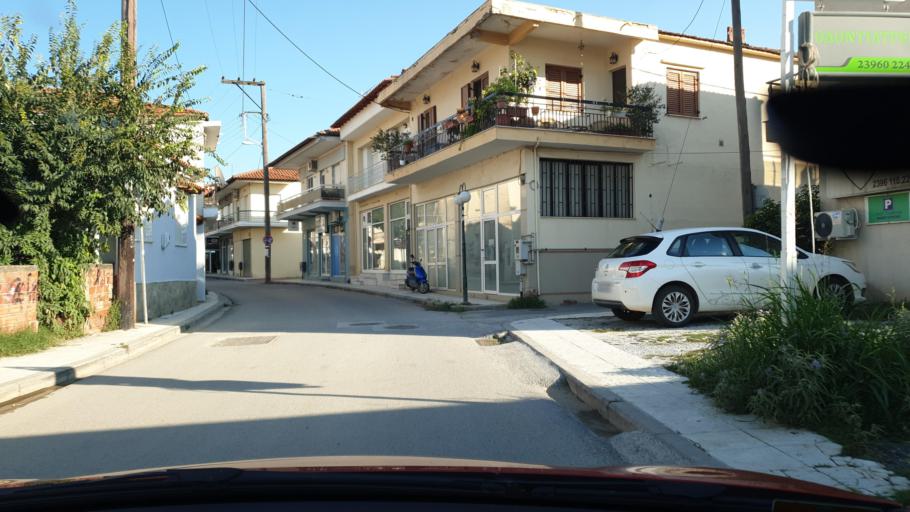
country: GR
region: Central Macedonia
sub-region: Nomos Thessalonikis
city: Vasilika
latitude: 40.4800
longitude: 23.1344
